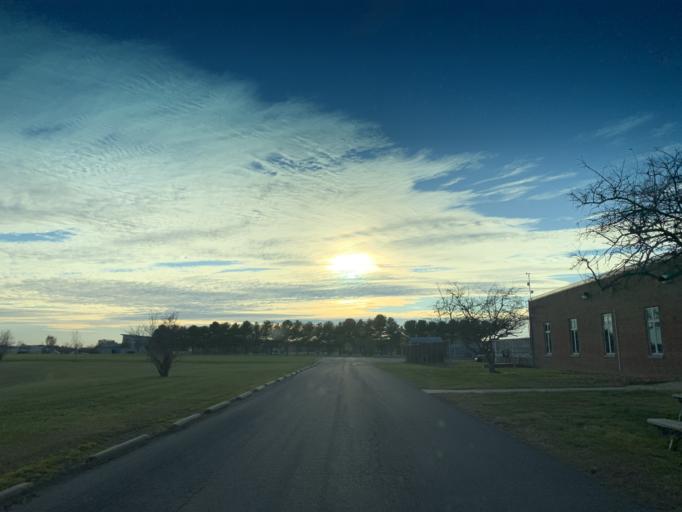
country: US
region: Maryland
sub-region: Kent County
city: Chestertown
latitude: 39.2843
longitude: -76.0905
